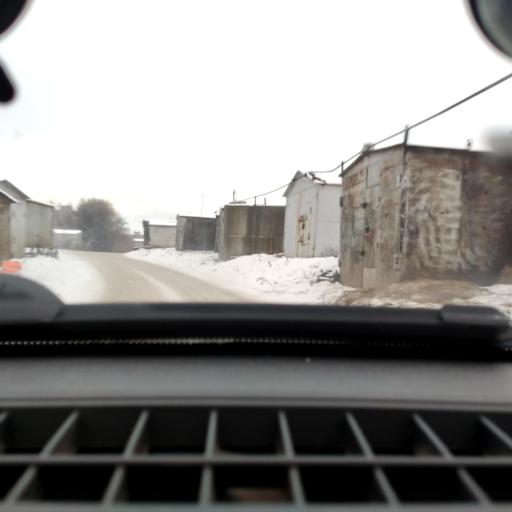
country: RU
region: Bashkortostan
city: Ufa
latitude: 54.8073
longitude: 56.1402
